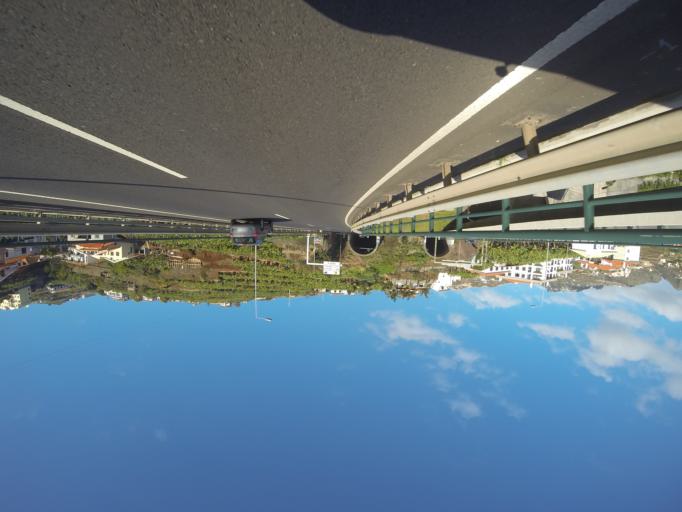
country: PT
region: Madeira
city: Camara de Lobos
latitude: 32.6602
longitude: -16.9763
